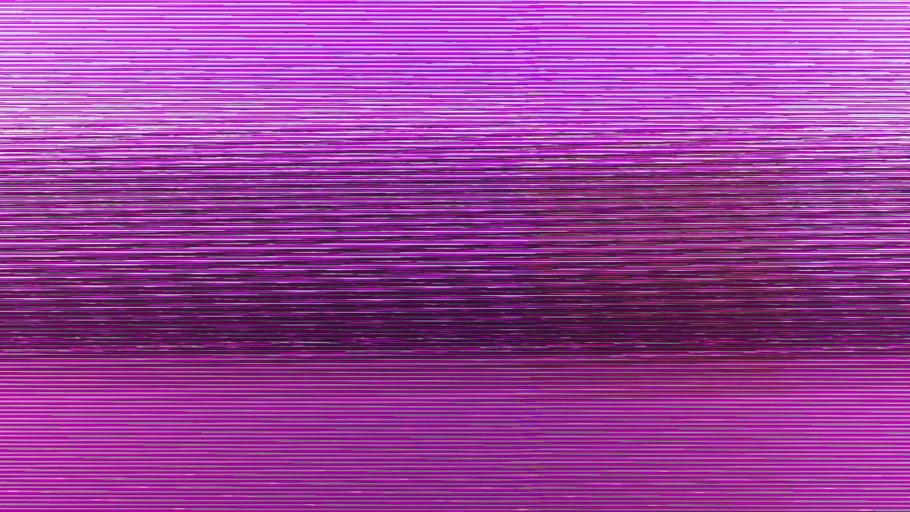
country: US
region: Michigan
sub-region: Genesee County
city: Grand Blanc
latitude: 42.9450
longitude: -83.6297
